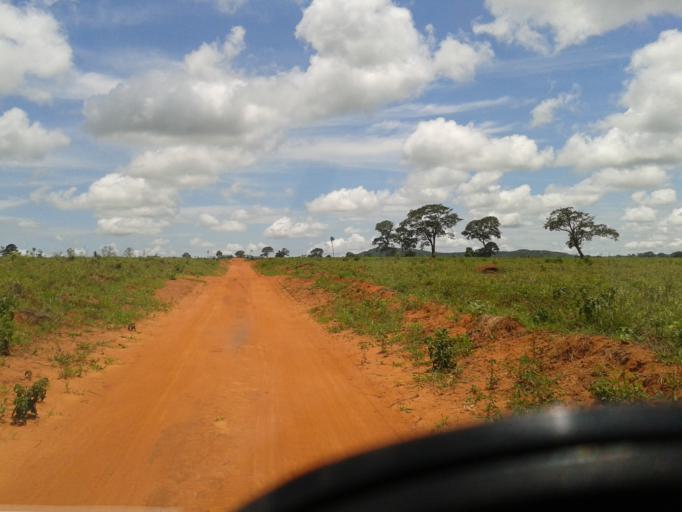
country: BR
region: Minas Gerais
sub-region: Santa Vitoria
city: Santa Vitoria
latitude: -19.0102
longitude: -49.9253
